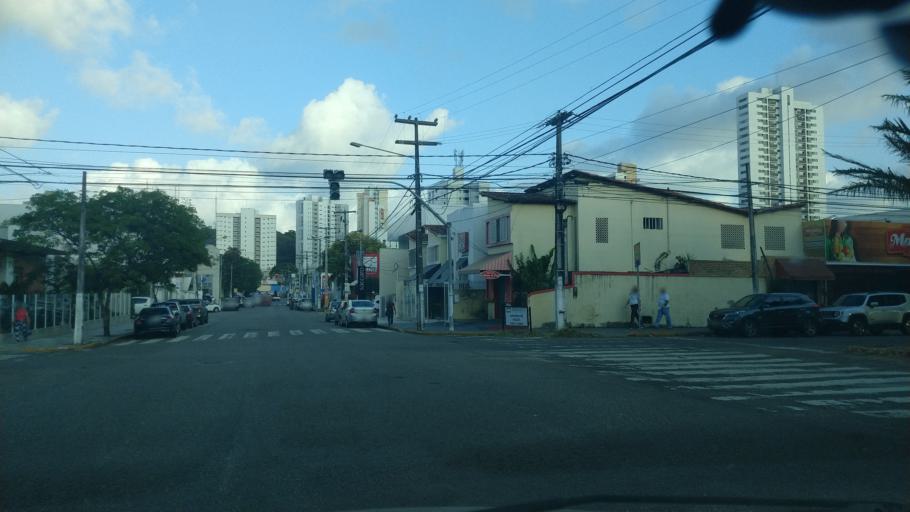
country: BR
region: Rio Grande do Norte
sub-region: Natal
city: Natal
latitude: -5.7882
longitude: -35.1988
